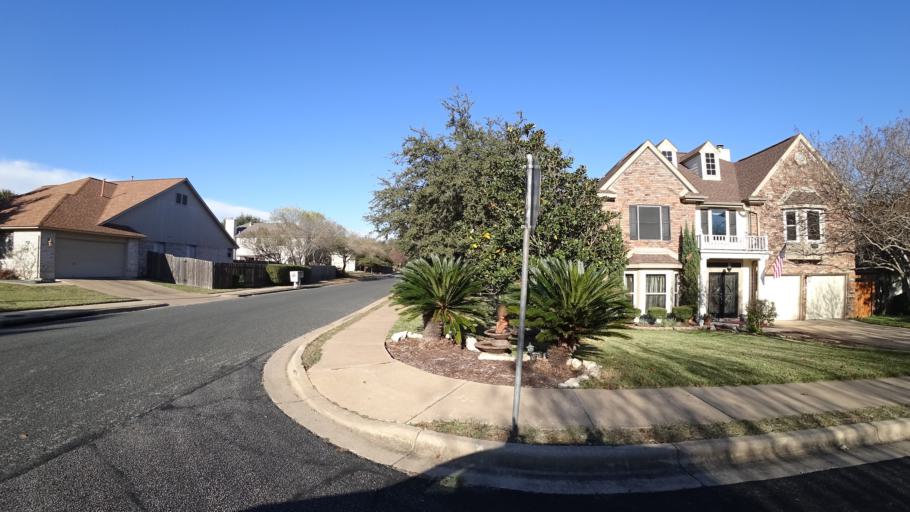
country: US
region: Texas
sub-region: Williamson County
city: Brushy Creek
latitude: 30.4913
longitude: -97.7429
